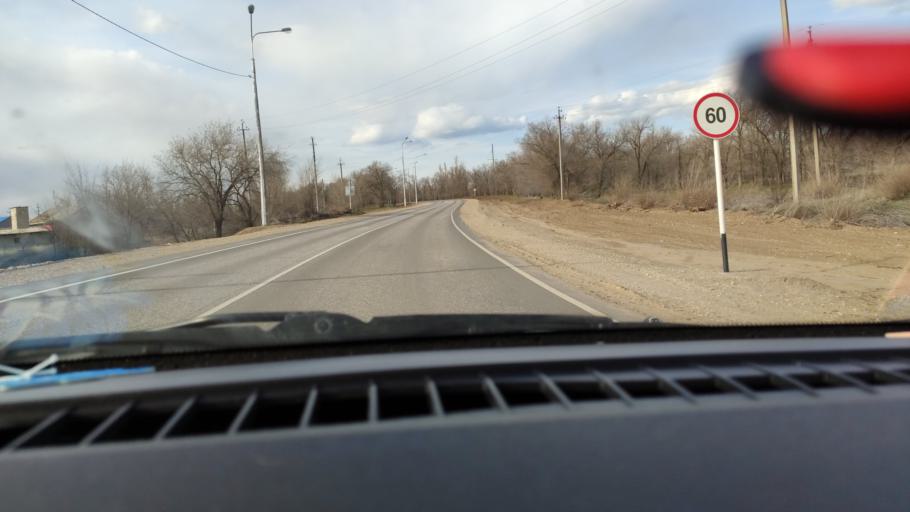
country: RU
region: Saratov
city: Krasnoarmeysk
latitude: 51.0901
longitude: 45.9572
